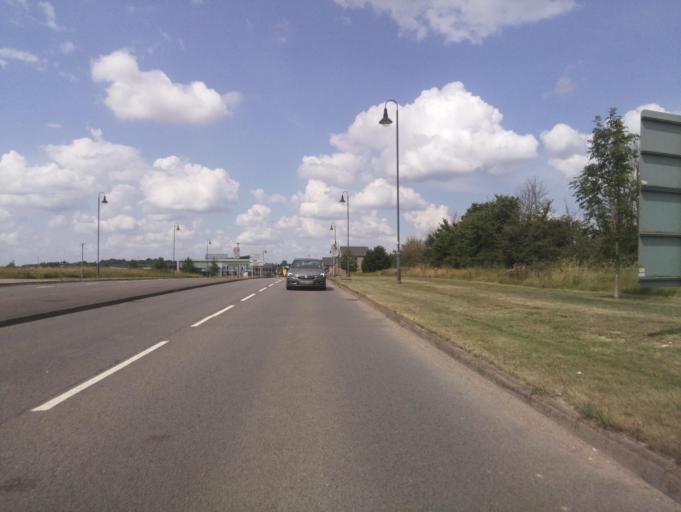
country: GB
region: England
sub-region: Borough of Swindon
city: Wroughton
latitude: 51.5440
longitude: -1.8038
